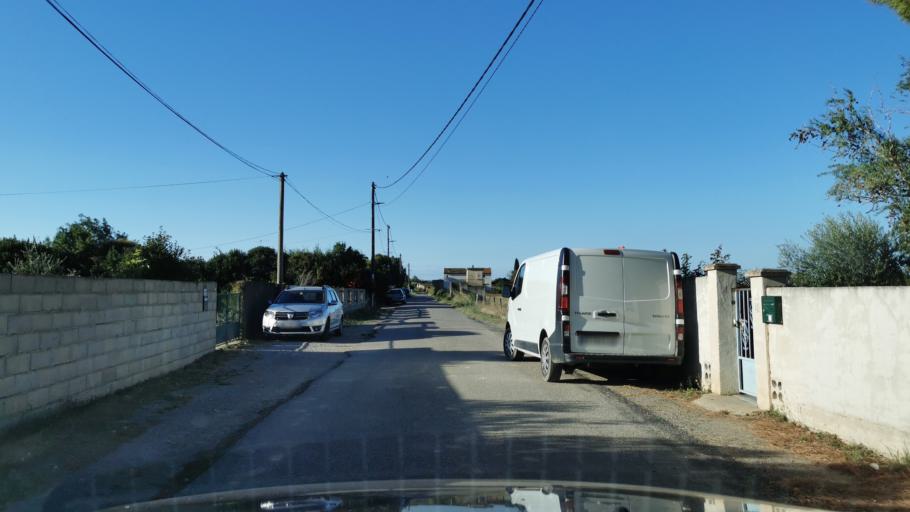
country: FR
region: Languedoc-Roussillon
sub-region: Departement de l'Aude
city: Coursan
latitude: 43.2605
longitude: 3.0221
